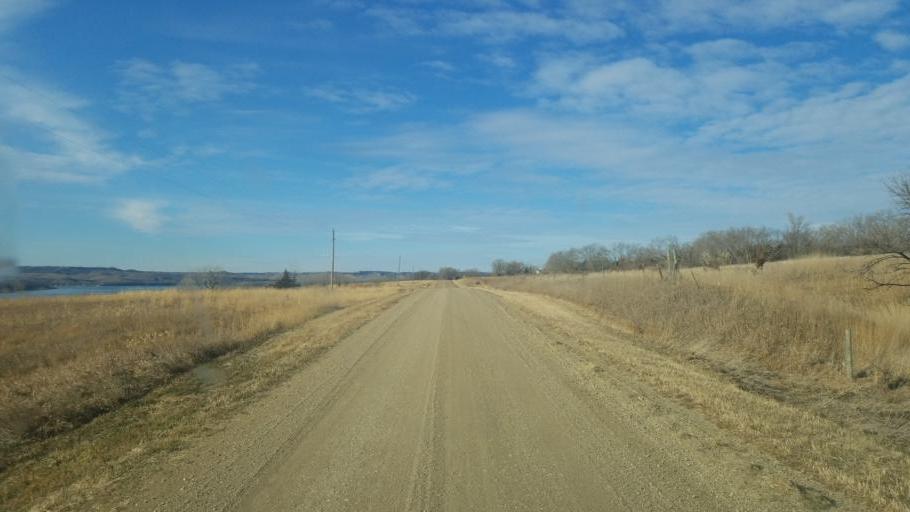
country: US
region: South Dakota
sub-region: Charles Mix County
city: Wagner
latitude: 42.9279
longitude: -98.4023
